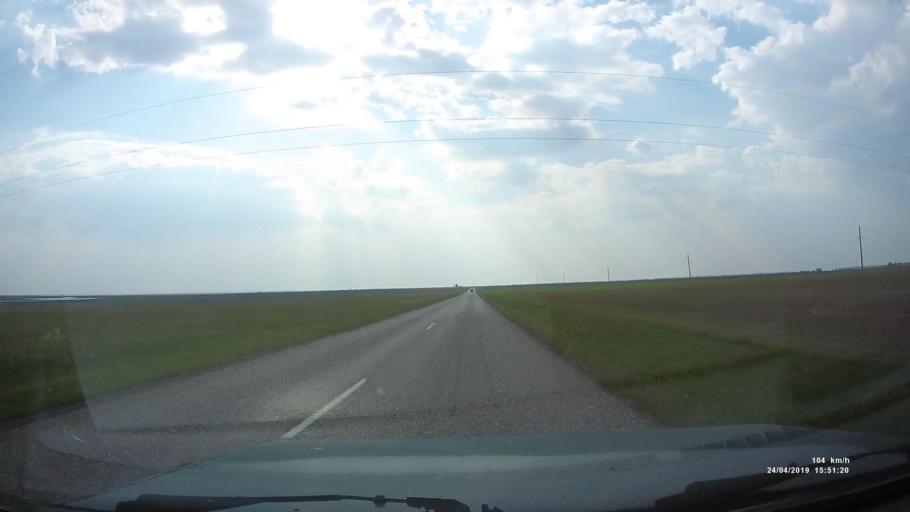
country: RU
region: Kalmykiya
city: Yashalta
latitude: 46.6043
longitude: 42.6132
